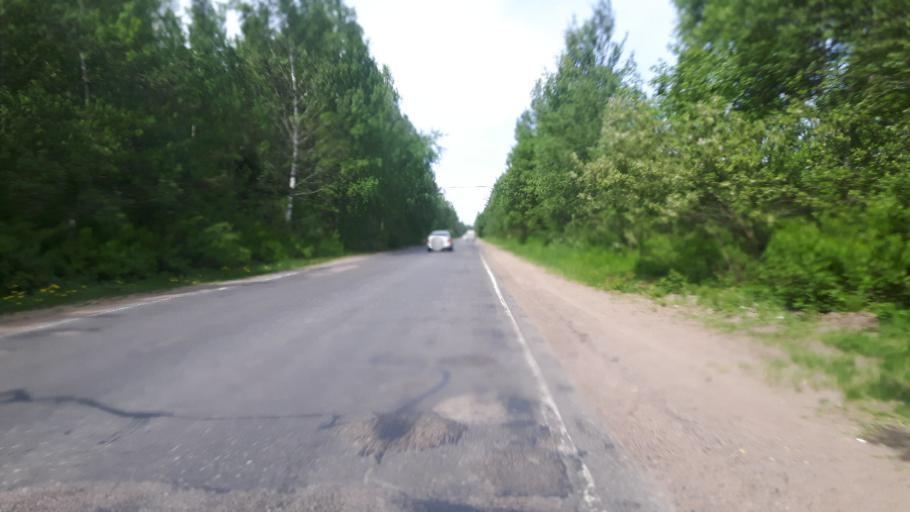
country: RU
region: Leningrad
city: Ust'-Luga
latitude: 59.6410
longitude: 28.2765
